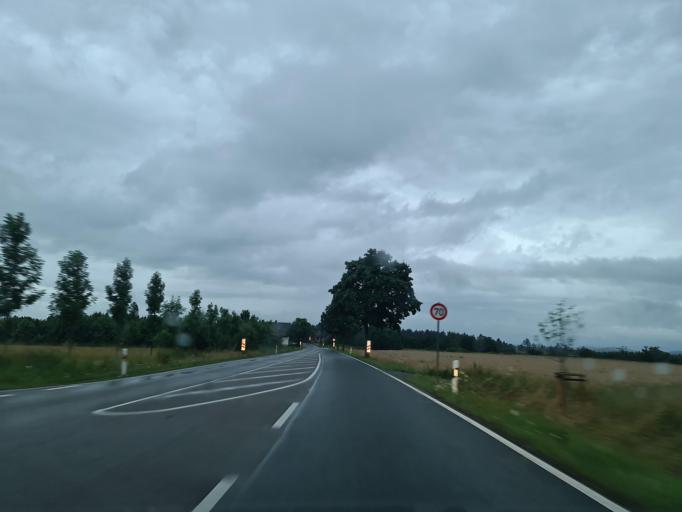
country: DE
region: Saxony
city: Limbach
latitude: 50.5428
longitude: 12.2571
